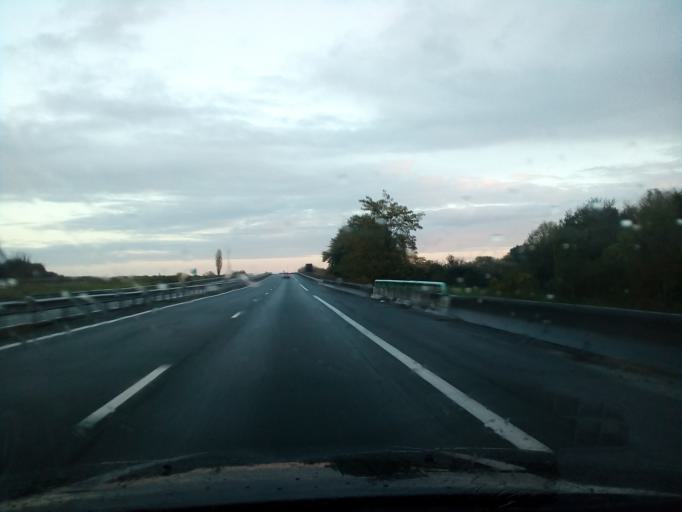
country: FR
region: Aquitaine
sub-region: Departement de la Gironde
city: Cavignac
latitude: 45.0903
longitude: -0.3818
